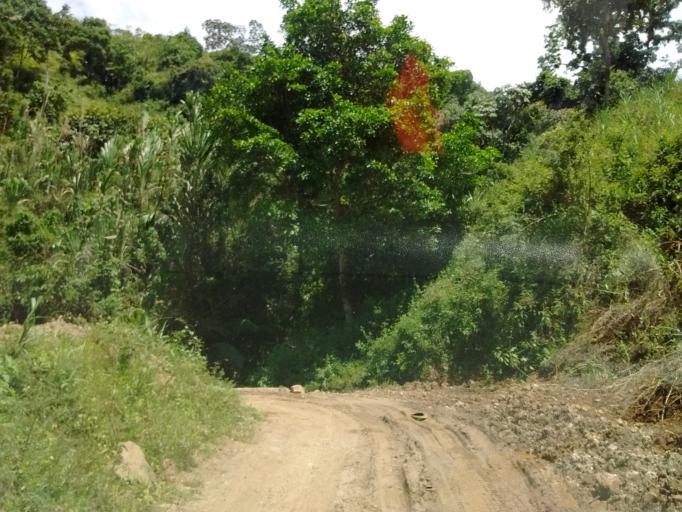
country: CO
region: Cauca
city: Morales
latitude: 2.6704
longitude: -76.7661
